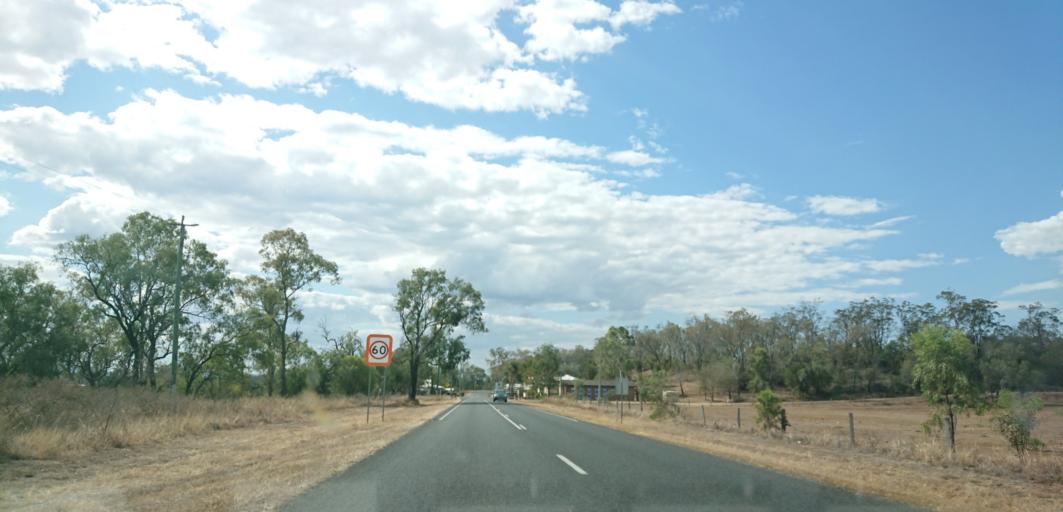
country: AU
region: Queensland
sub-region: Lockyer Valley
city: Gatton
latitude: -27.6333
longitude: 152.1870
